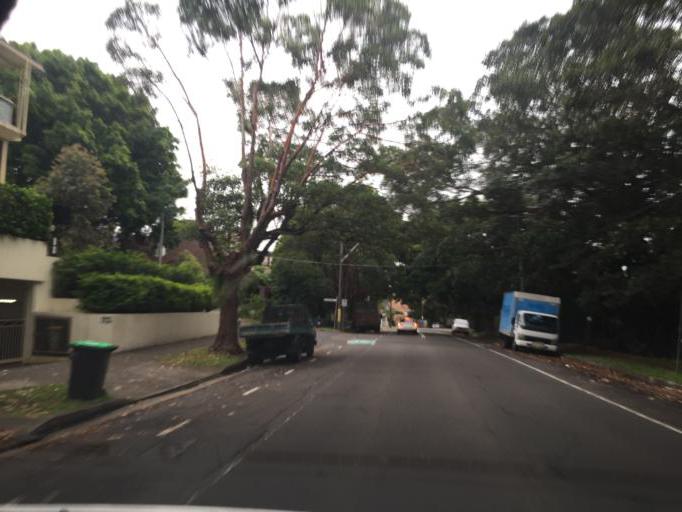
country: AU
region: New South Wales
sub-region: Waverley
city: Bondi Beach
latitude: -33.8834
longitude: 151.2654
